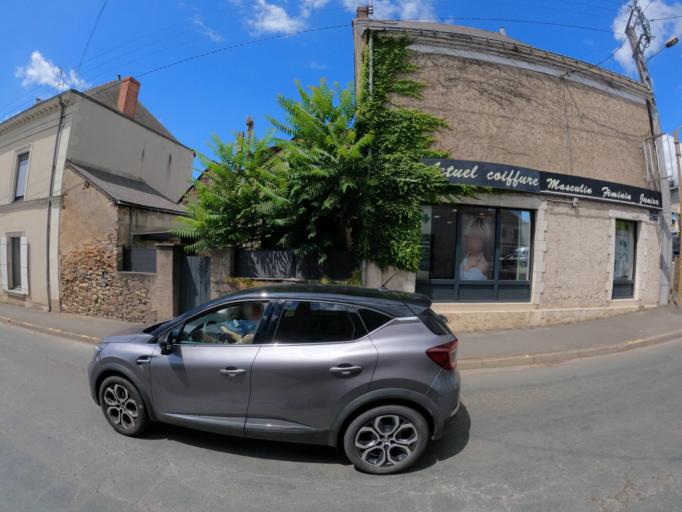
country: FR
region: Pays de la Loire
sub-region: Departement de Maine-et-Loire
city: Champigne
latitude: 47.6636
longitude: -0.5722
